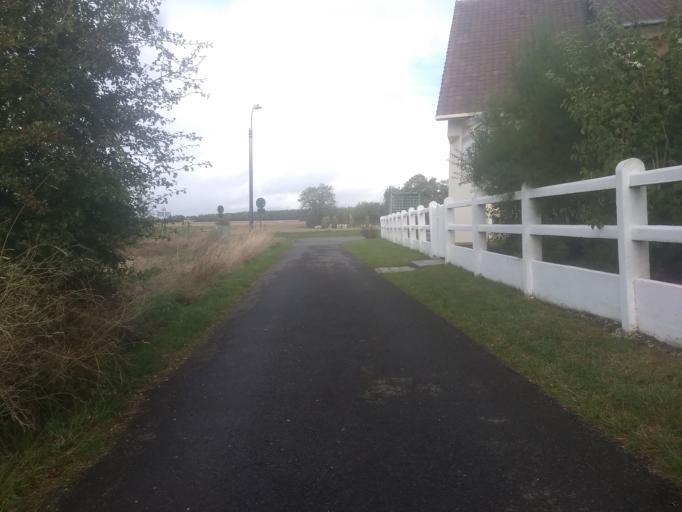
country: FR
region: Nord-Pas-de-Calais
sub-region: Departement du Pas-de-Calais
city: Dainville
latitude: 50.2817
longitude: 2.7130
